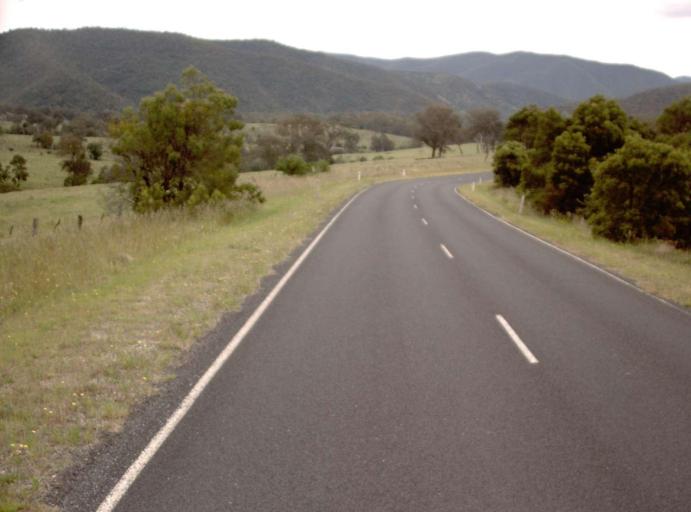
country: AU
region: Victoria
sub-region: East Gippsland
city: Bairnsdale
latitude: -37.5675
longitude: 147.1869
